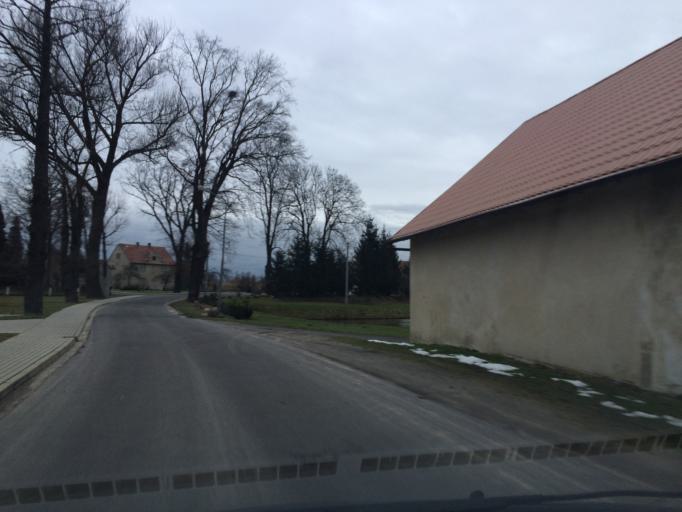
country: PL
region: Lower Silesian Voivodeship
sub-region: Powiat lubanski
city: Pisarzowice
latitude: 51.1651
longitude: 15.2539
